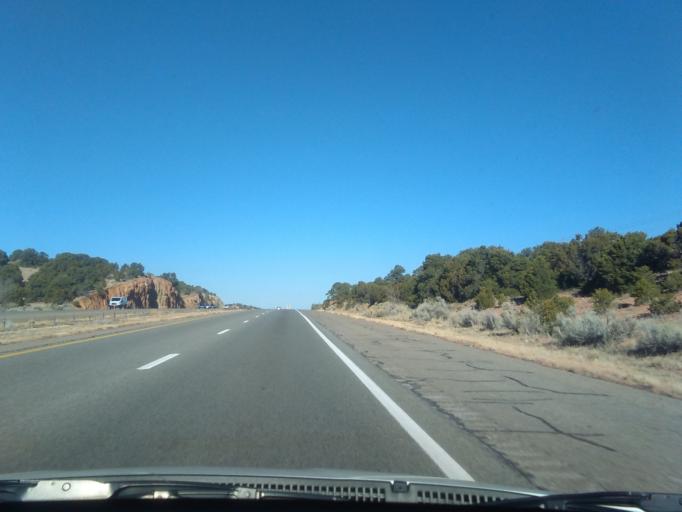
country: US
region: New Mexico
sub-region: Santa Fe County
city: Santa Fe
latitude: 35.6114
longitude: -105.9152
